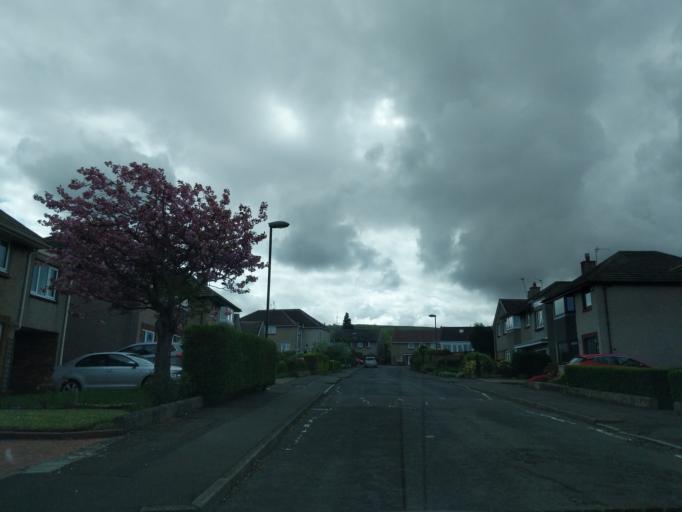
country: GB
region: Scotland
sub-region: Edinburgh
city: Currie
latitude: 55.9014
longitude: -3.2975
